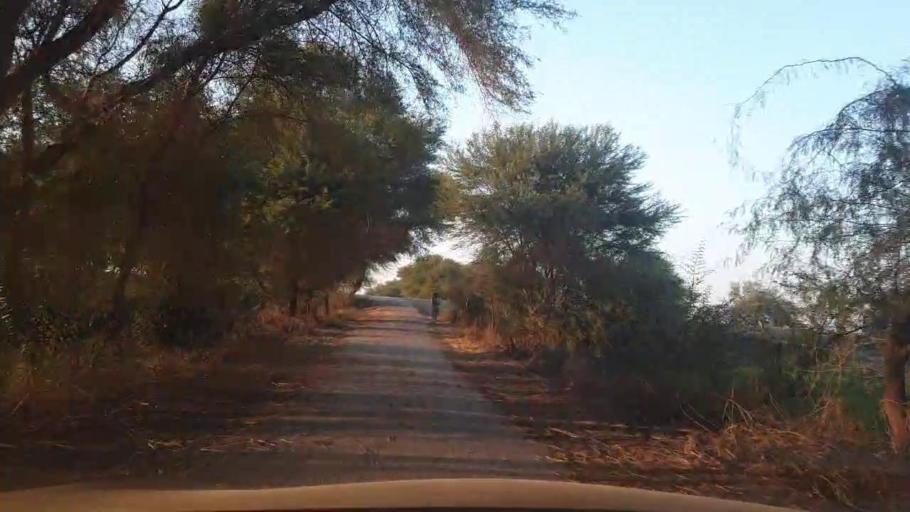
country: PK
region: Sindh
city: Ubauro
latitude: 28.1877
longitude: 69.6014
